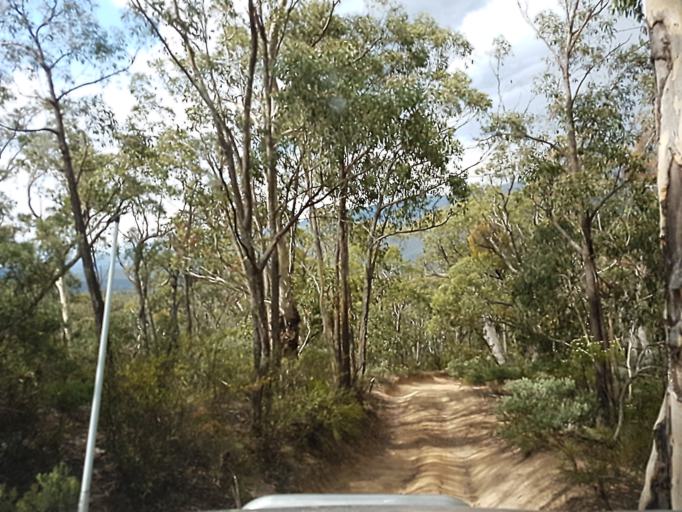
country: AU
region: New South Wales
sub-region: Snowy River
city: Jindabyne
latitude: -36.8782
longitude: 148.2172
